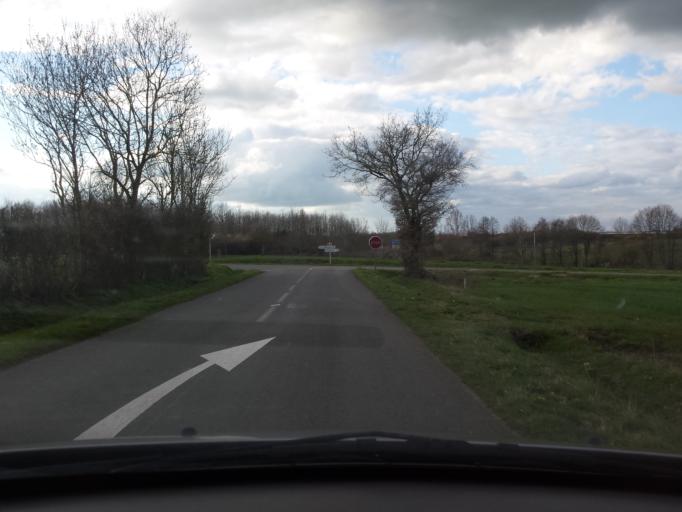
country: FR
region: Pays de la Loire
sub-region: Departement de la Vendee
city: Saint-Martin-des-Noyers
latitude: 46.7250
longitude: -1.1551
